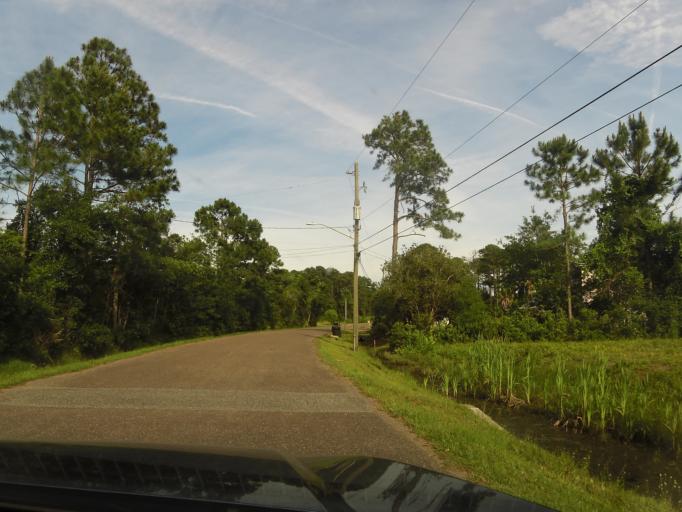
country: US
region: Florida
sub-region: Nassau County
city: Fernandina Beach
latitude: 30.5117
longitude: -81.4827
